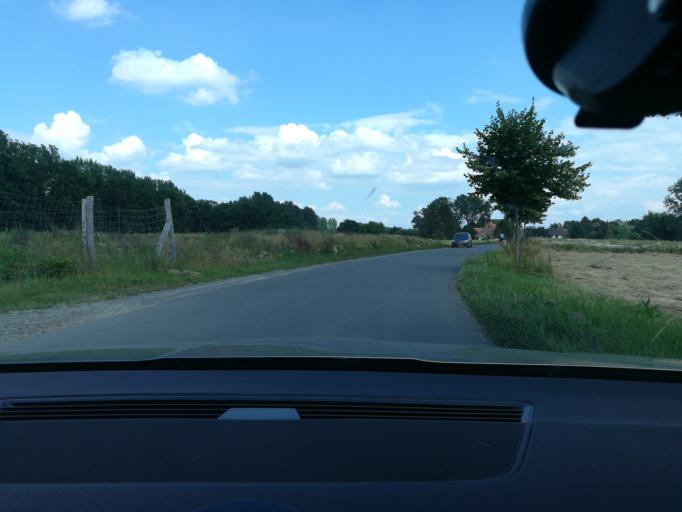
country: DE
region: North Rhine-Westphalia
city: Lubbecke
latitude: 52.3325
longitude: 8.6319
